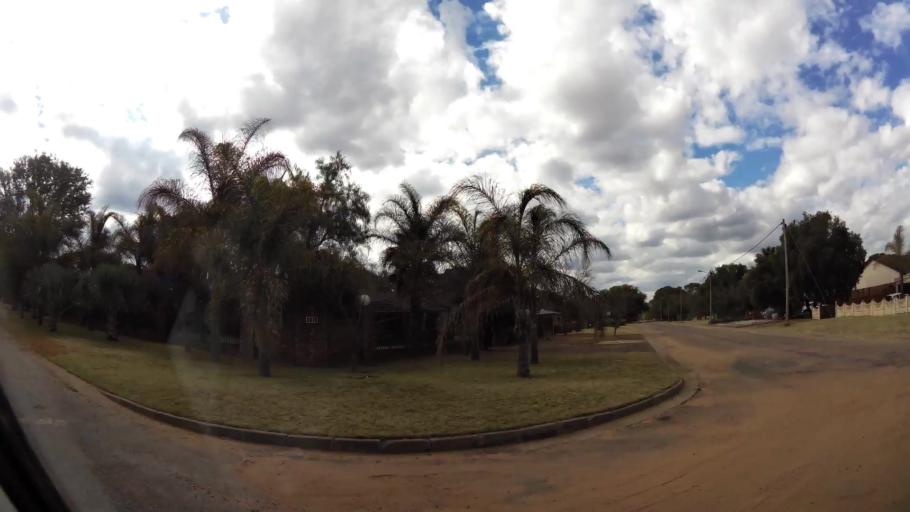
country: ZA
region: Limpopo
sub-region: Waterberg District Municipality
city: Modimolle
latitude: -24.7114
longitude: 28.4027
